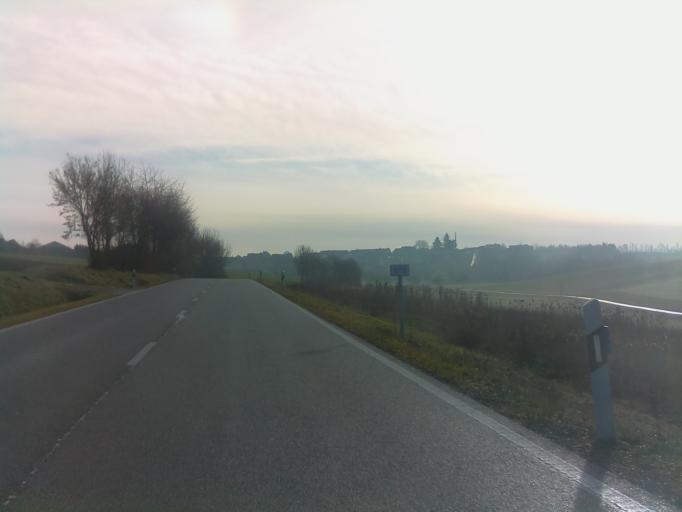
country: DE
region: Bavaria
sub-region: Regierungsbezirk Unterfranken
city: Waldbrunn
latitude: 49.7664
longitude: 9.7898
